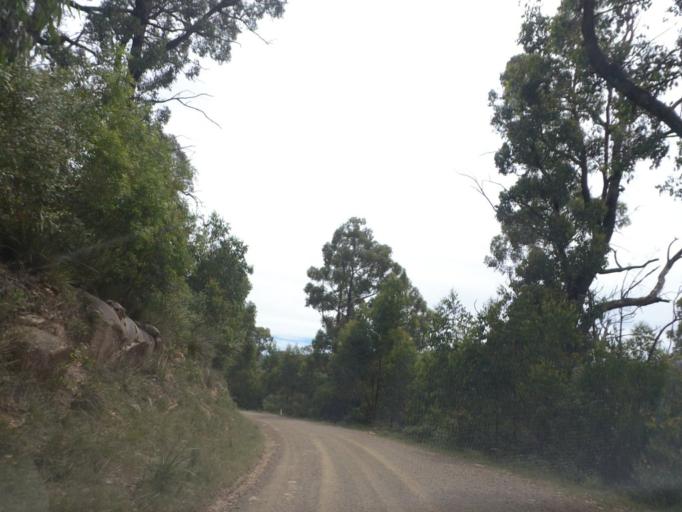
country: AU
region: Victoria
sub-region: Yarra Ranges
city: Healesville
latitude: -37.4497
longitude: 145.5786
